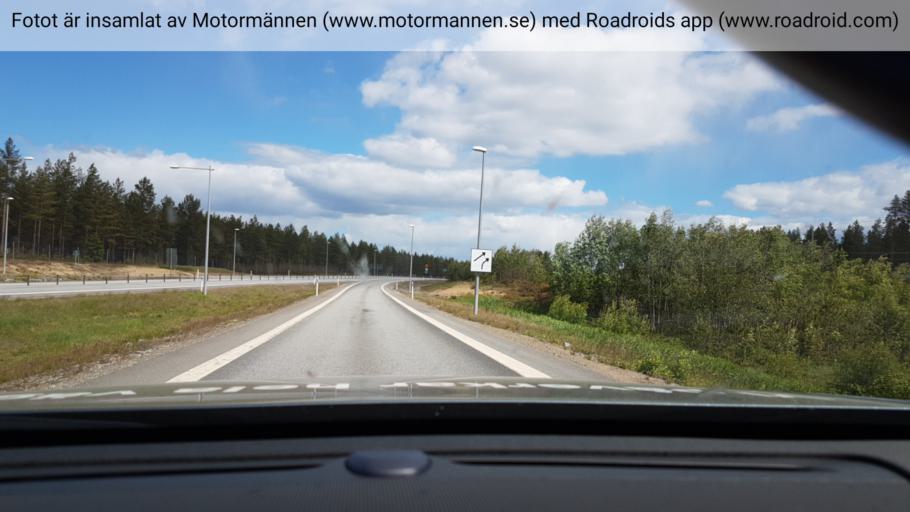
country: SE
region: Vaesterbotten
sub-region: Nordmalings Kommun
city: Nordmaling
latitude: 63.5827
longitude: 19.5380
